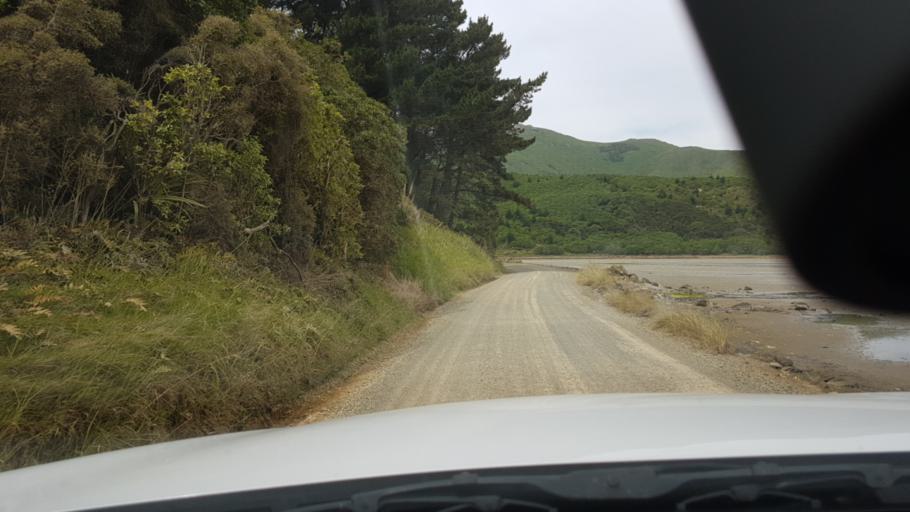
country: NZ
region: Otago
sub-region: Dunedin City
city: Portobello
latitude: -45.8571
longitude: 170.6790
